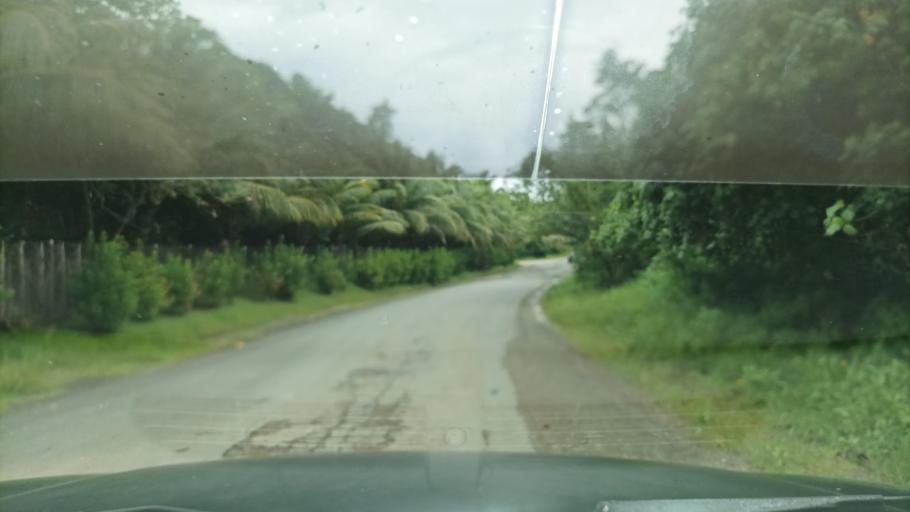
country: FM
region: Yap
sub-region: Weloy Municipality
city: Colonia
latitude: 9.5467
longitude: 138.1542
